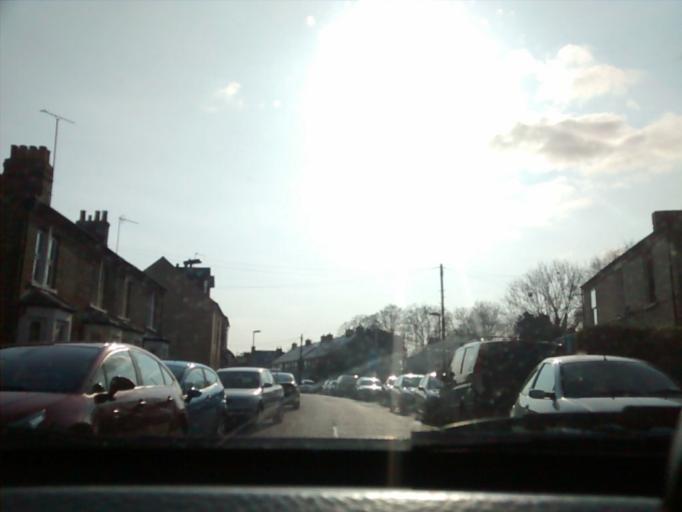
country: GB
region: England
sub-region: Cambridgeshire
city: Cambridge
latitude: 52.2151
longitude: 0.1559
